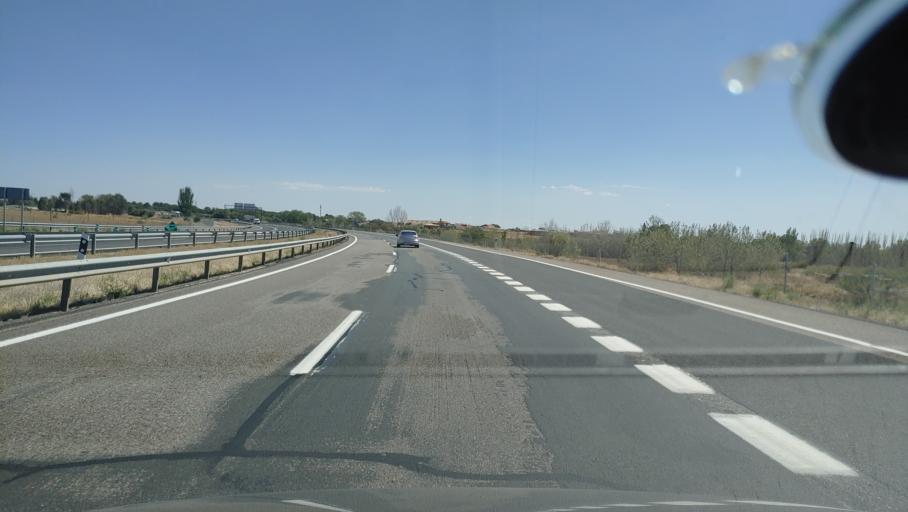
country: ES
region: Castille-La Mancha
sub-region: Provincia de Ciudad Real
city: Villarta de San Juan
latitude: 39.2477
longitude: -3.4291
